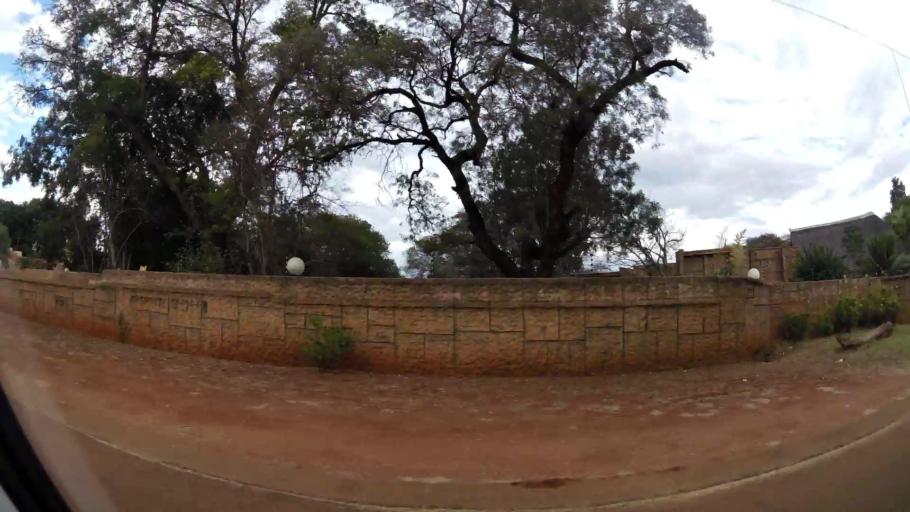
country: ZA
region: Limpopo
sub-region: Waterberg District Municipality
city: Modimolle
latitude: -24.5109
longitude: 28.7150
